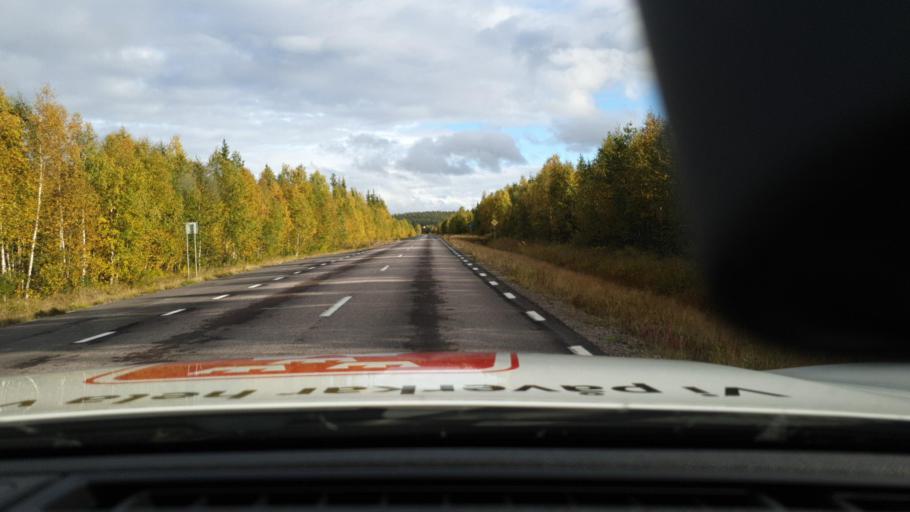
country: SE
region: Norrbotten
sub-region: Overkalix Kommun
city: OEverkalix
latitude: 66.9761
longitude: 22.6319
